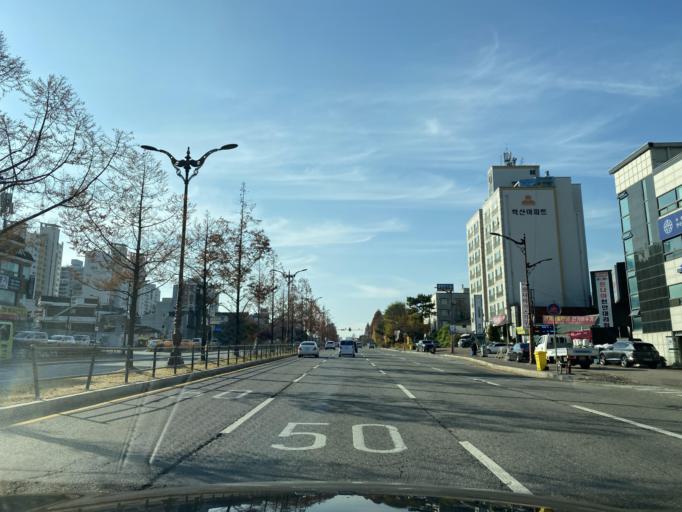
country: KR
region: Chungcheongnam-do
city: Cheonan
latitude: 36.7987
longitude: 127.1408
